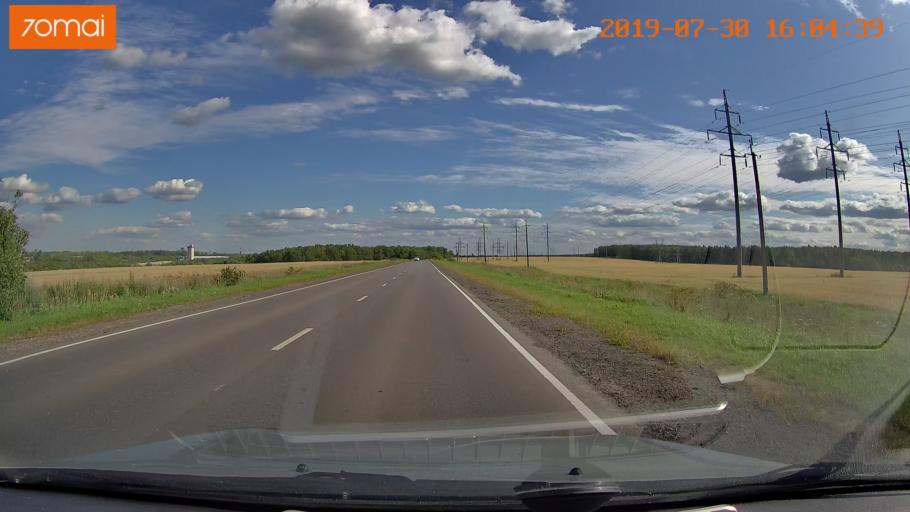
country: RU
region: Moskovskaya
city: Lopatinskiy
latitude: 55.2782
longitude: 38.7092
